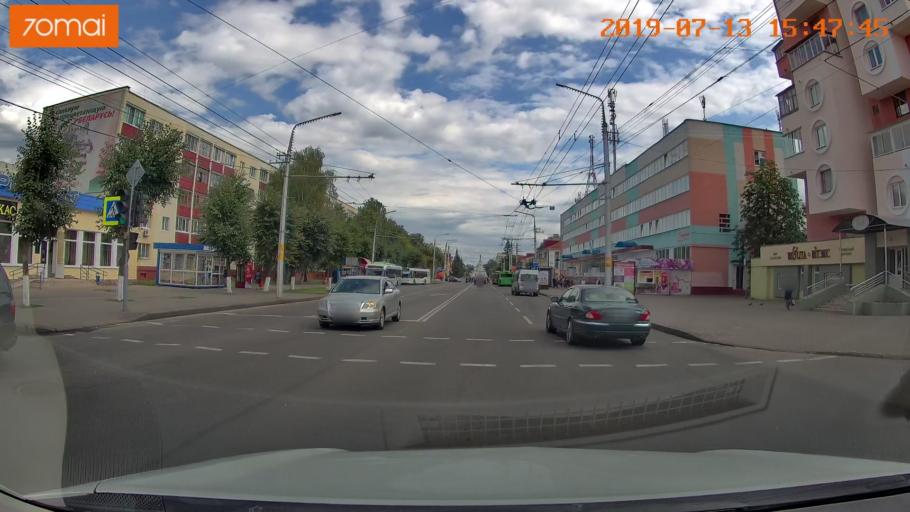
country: BY
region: Mogilev
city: Babruysk
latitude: 53.1490
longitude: 29.2292
